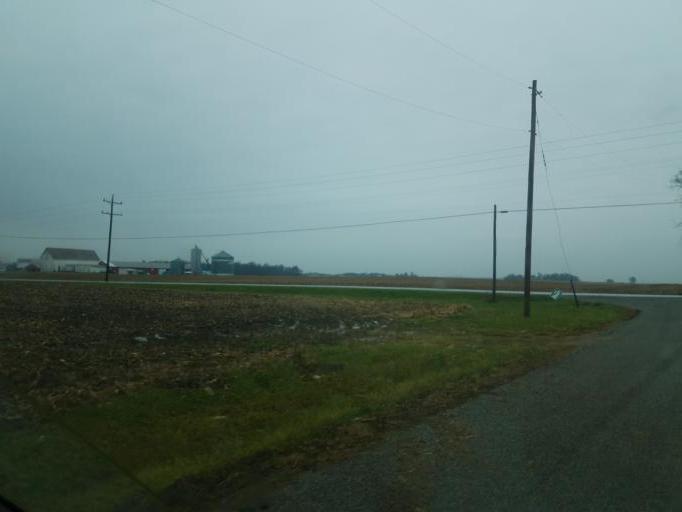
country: US
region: Ohio
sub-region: Knox County
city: Centerburg
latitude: 40.2447
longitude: -82.7229
